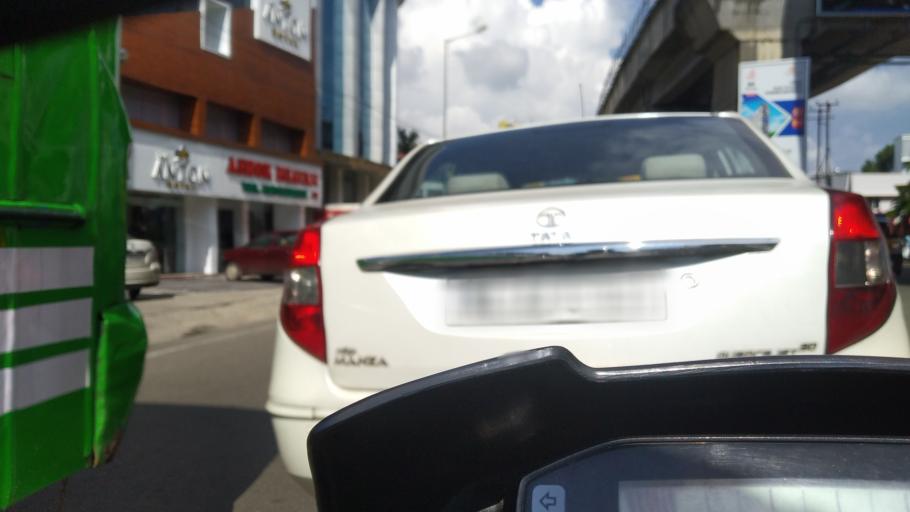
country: IN
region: Kerala
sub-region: Ernakulam
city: Cochin
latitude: 9.9861
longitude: 76.2825
